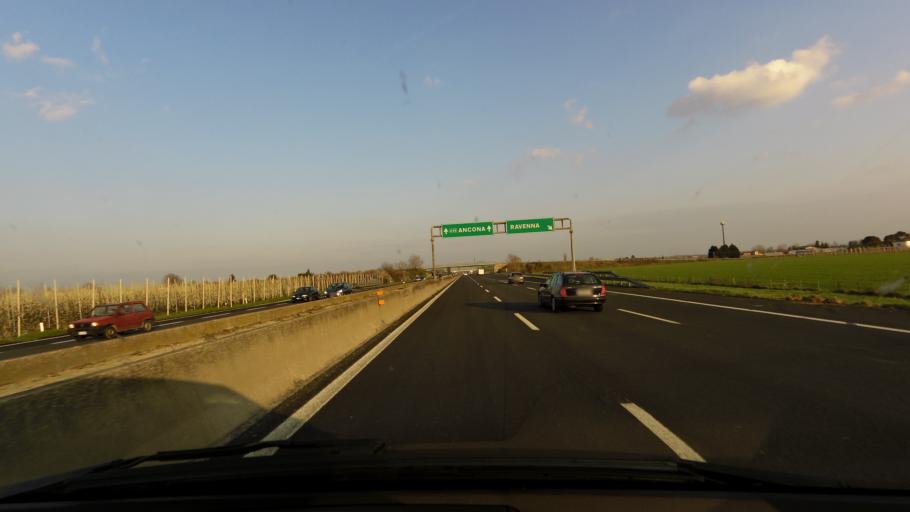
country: IT
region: Emilia-Romagna
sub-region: Provincia di Ravenna
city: Castel Bolognese
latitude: 44.3570
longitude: 11.8057
